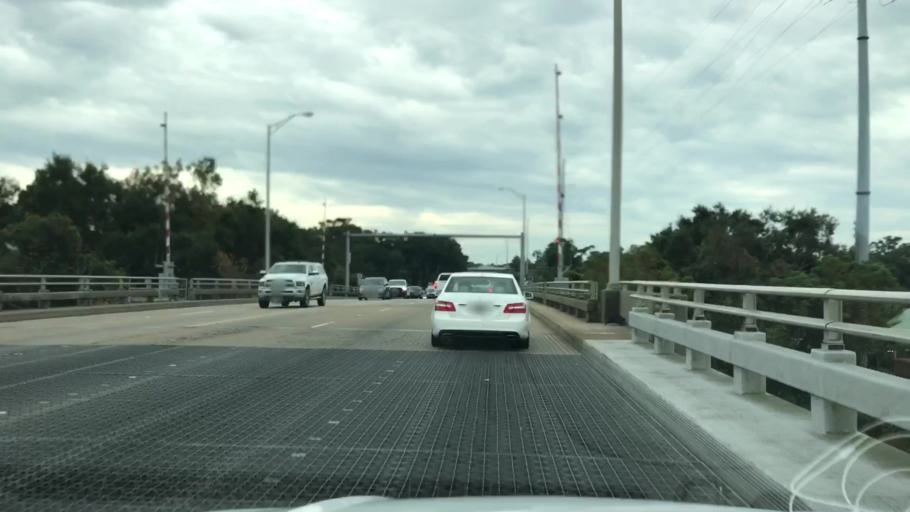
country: US
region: South Carolina
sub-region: Charleston County
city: Charleston
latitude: 32.7663
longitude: -79.9742
